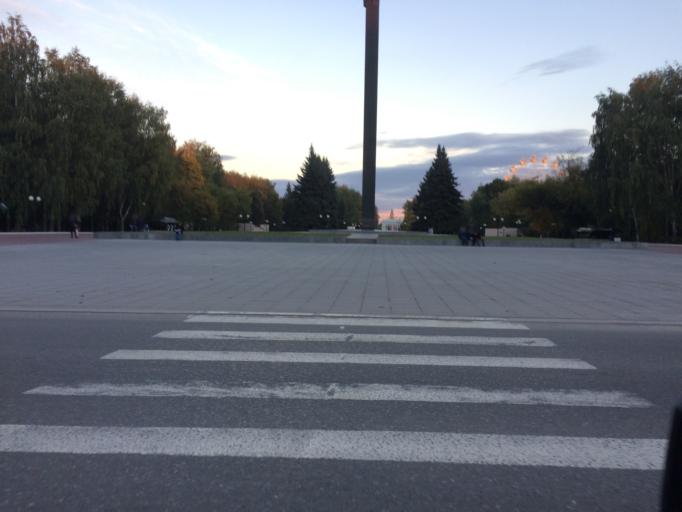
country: RU
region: Mariy-El
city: Yoshkar-Ola
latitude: 56.6373
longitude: 47.8865
